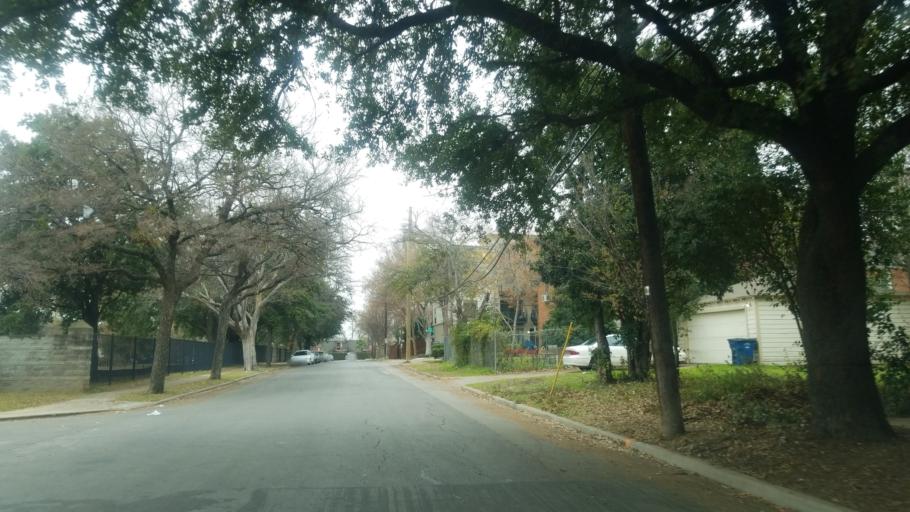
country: US
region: Texas
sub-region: Dallas County
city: Highland Park
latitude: 32.8158
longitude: -96.8202
